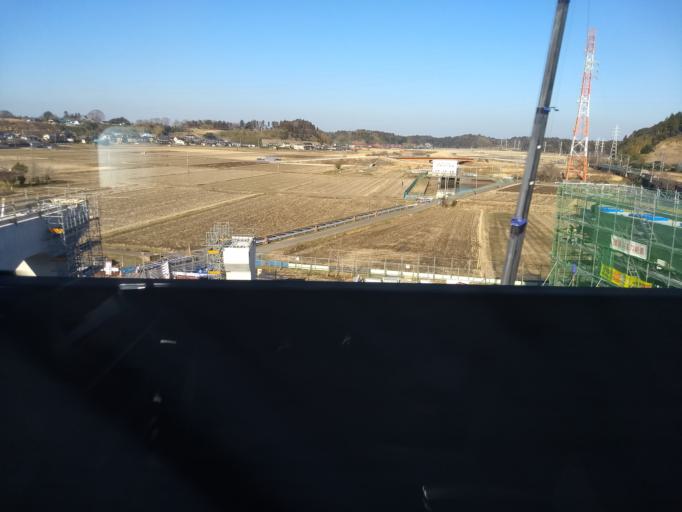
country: JP
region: Chiba
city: Narita
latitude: 35.7974
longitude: 140.3146
